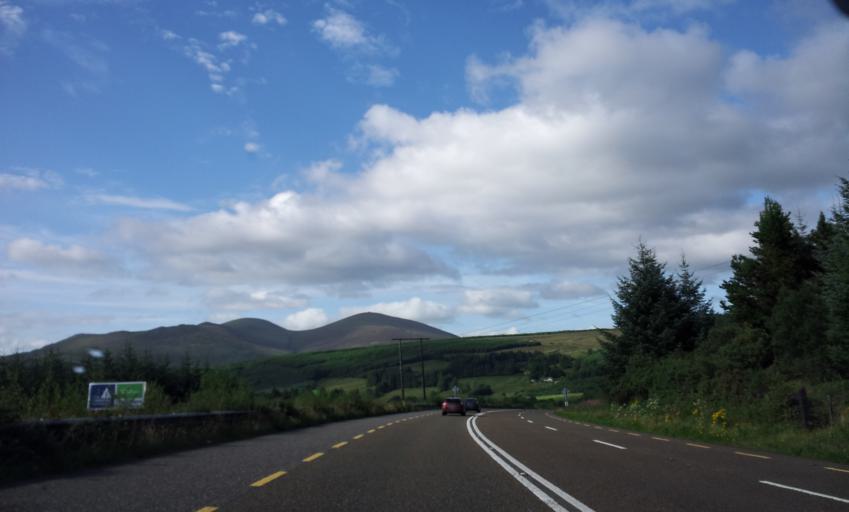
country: IE
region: Munster
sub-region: County Cork
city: Millstreet
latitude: 51.9720
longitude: -9.2528
